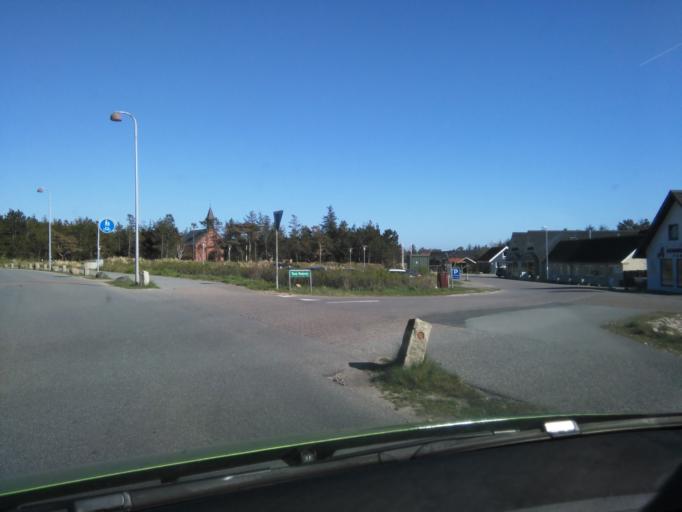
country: DK
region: South Denmark
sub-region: Varde Kommune
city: Oksbol
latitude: 55.5558
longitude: 8.1362
